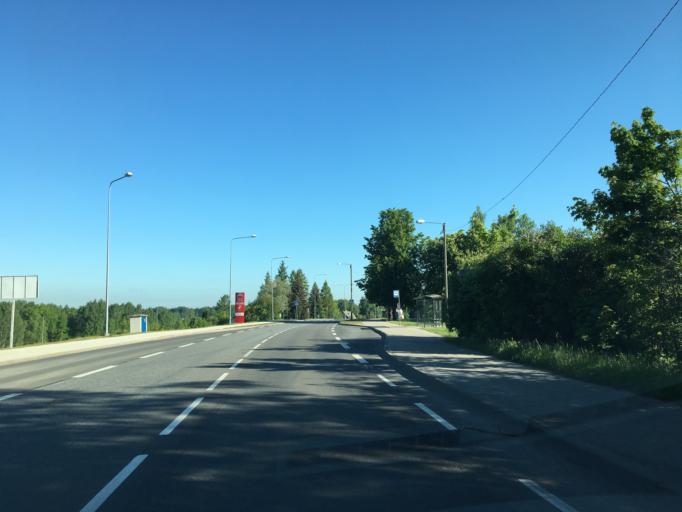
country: EE
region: Tartu
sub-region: Tartu linn
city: Tartu
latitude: 58.3985
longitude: 26.7092
